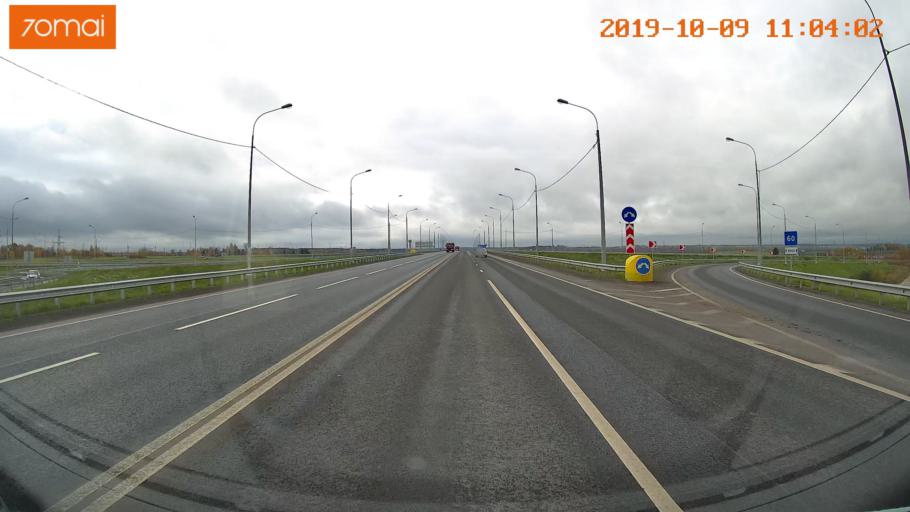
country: RU
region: Vologda
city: Vologda
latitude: 59.2162
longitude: 39.7722
